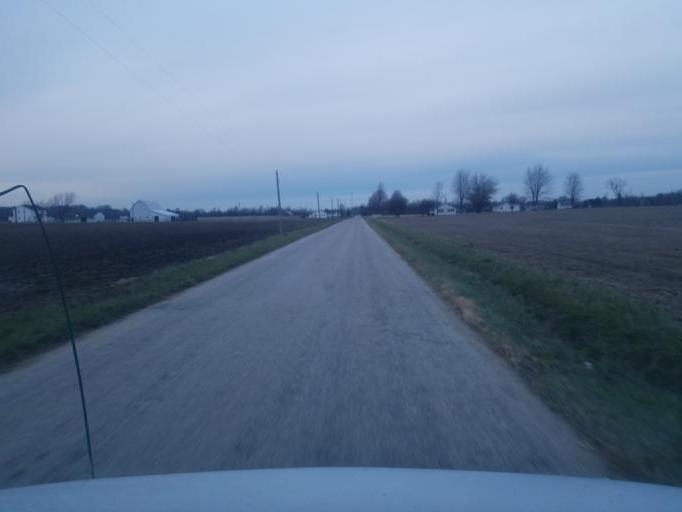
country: US
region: Indiana
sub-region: Adams County
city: Decatur
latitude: 40.7876
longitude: -84.8800
